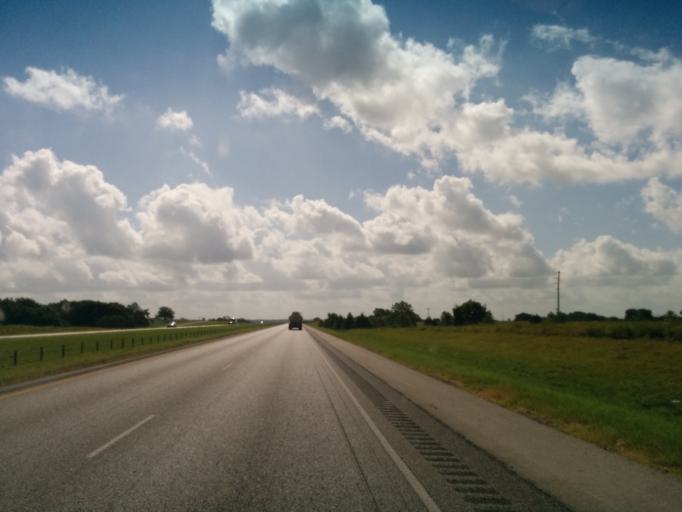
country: US
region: Texas
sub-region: Fayette County
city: Schulenburg
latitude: 29.6897
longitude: -96.9668
